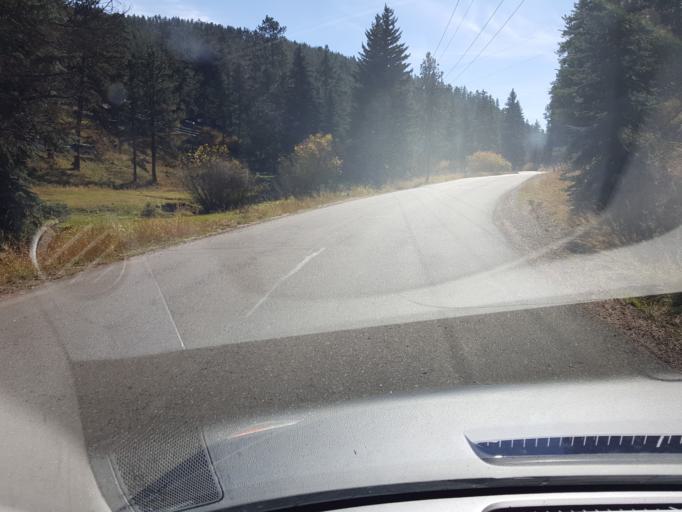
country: US
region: Colorado
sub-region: Jefferson County
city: Evergreen
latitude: 39.5891
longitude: -105.3446
